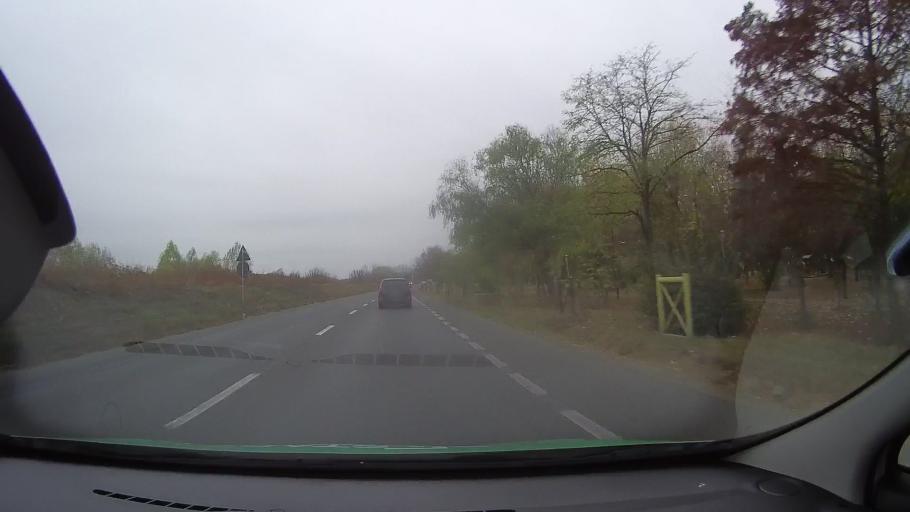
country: RO
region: Ialomita
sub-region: Comuna Slobozia
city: Slobozia
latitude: 44.5632
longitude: 27.3807
